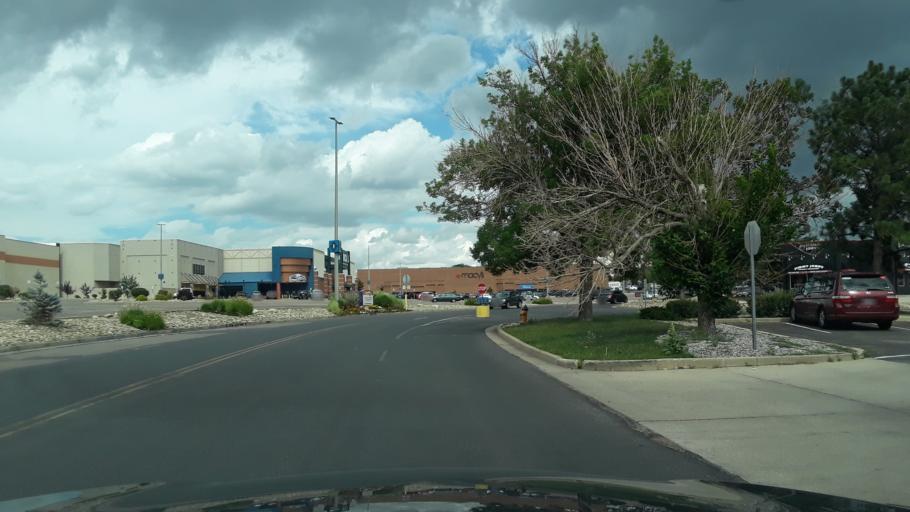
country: US
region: Colorado
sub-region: El Paso County
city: Air Force Academy
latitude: 38.9461
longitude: -104.7987
